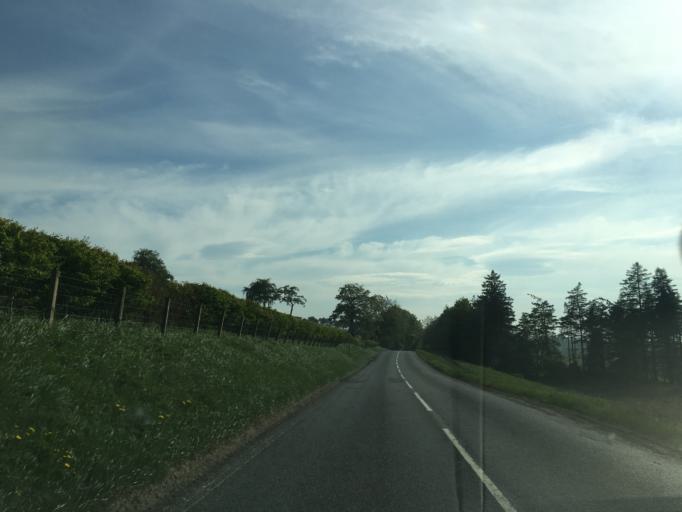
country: GB
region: Scotland
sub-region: Midlothian
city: Penicuik
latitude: 55.7786
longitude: -3.2313
